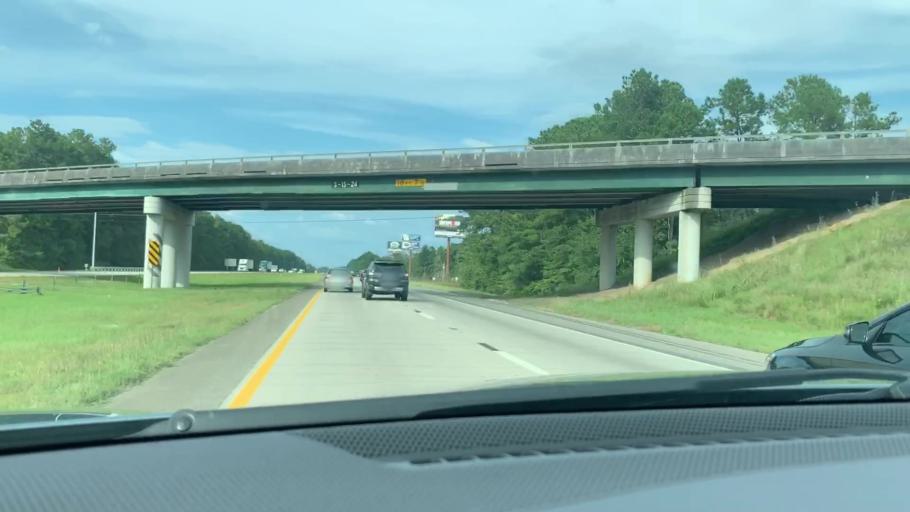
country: US
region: South Carolina
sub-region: Colleton County
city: Walterboro
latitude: 32.9412
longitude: -80.6850
